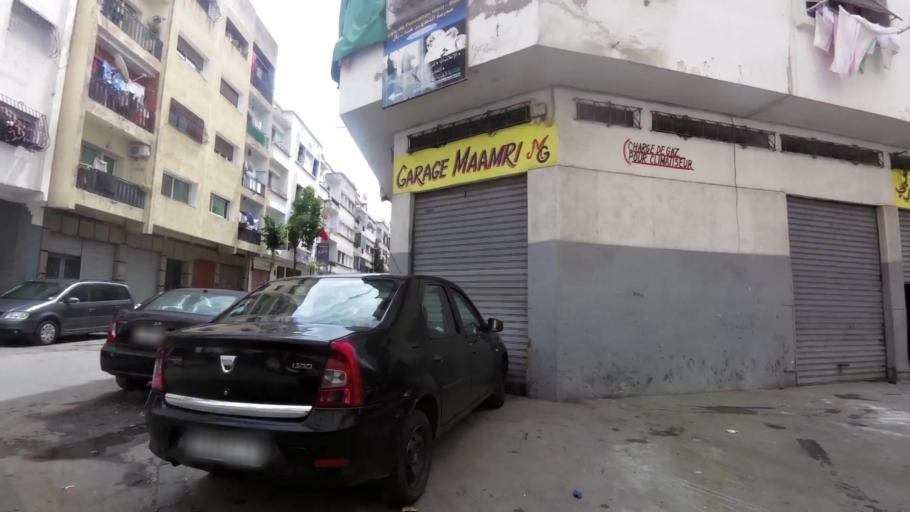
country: MA
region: Grand Casablanca
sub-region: Casablanca
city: Casablanca
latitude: 33.5964
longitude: -7.6280
